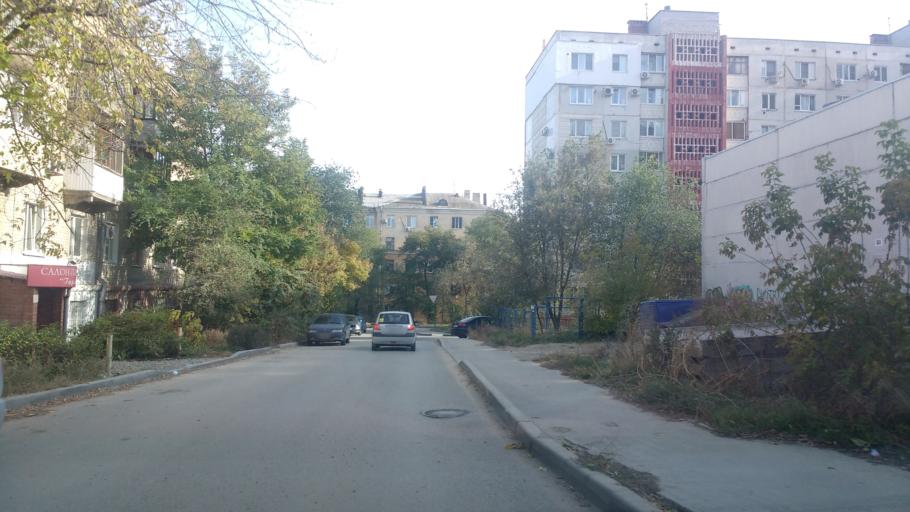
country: RU
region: Volgograd
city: Krasnoslobodsk
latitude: 48.7629
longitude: 44.5542
